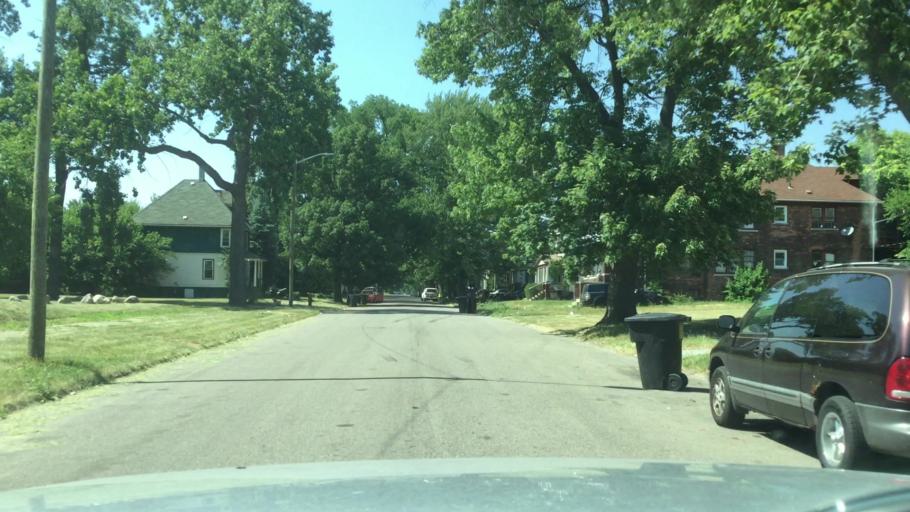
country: US
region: Michigan
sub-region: Wayne County
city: Detroit
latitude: 42.3639
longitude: -83.0169
